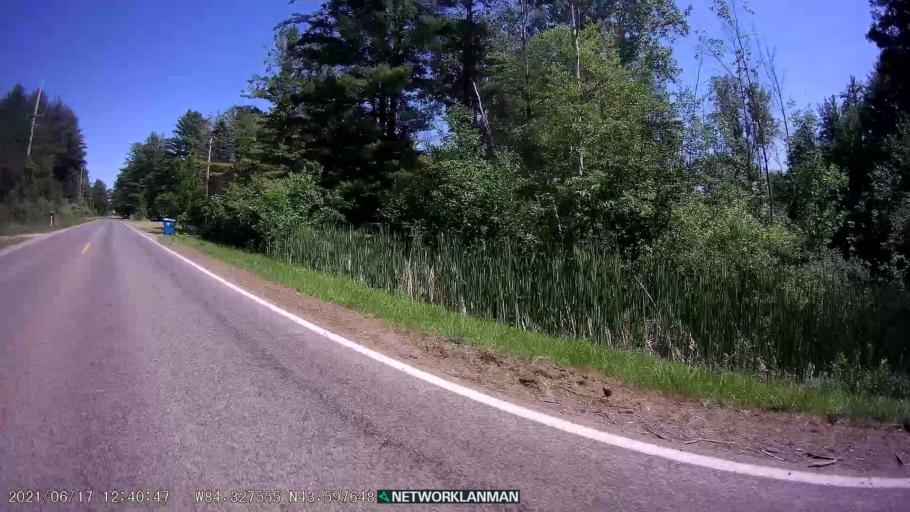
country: US
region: Michigan
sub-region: Midland County
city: Midland
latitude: 43.5976
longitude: -84.3275
